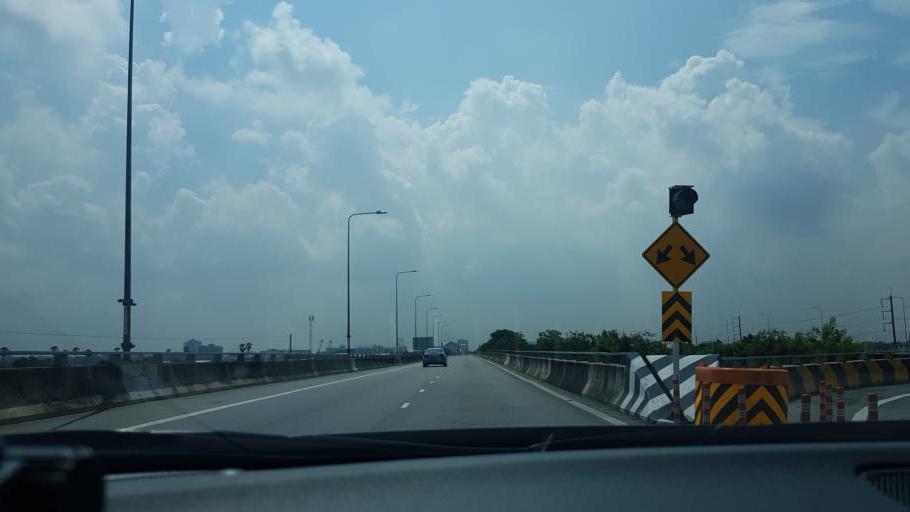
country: TH
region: Pathum Thani
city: Sam Khok
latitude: 14.0663
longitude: 100.5839
